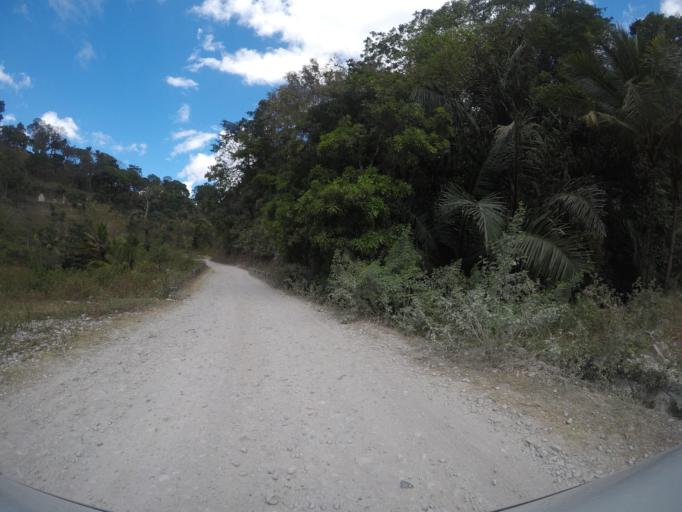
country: TL
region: Baucau
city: Baucau
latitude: -8.5259
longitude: 126.6902
